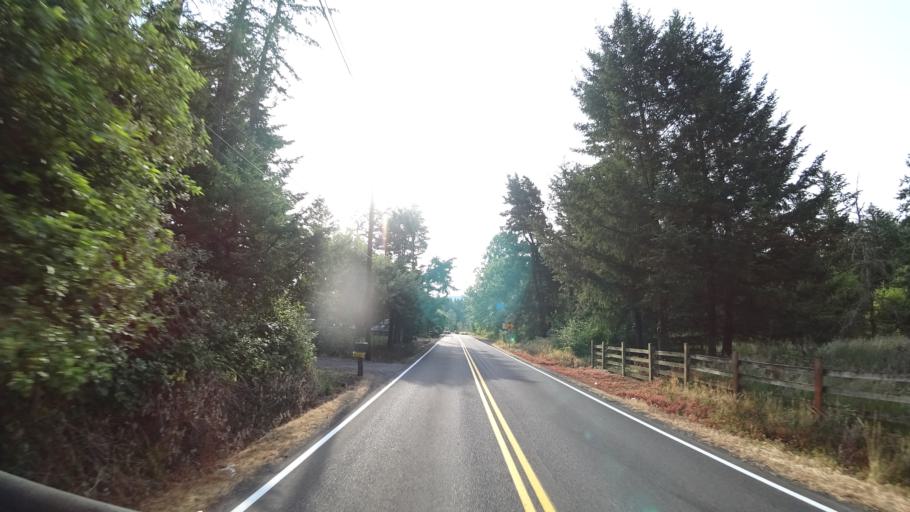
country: US
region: Oregon
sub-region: Clackamas County
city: Happy Valley
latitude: 45.4611
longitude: -122.4986
